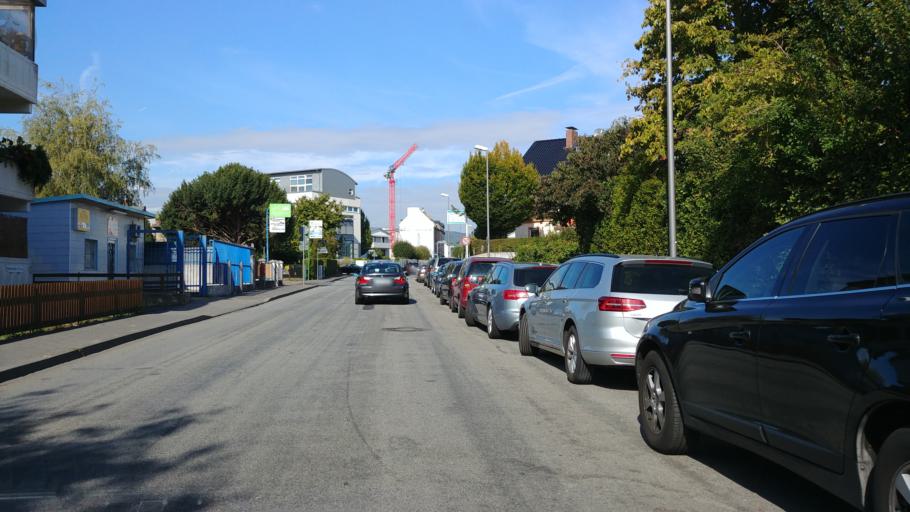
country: DE
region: Hesse
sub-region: Regierungsbezirk Darmstadt
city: Wiesbaden
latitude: 50.0748
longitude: 8.2093
